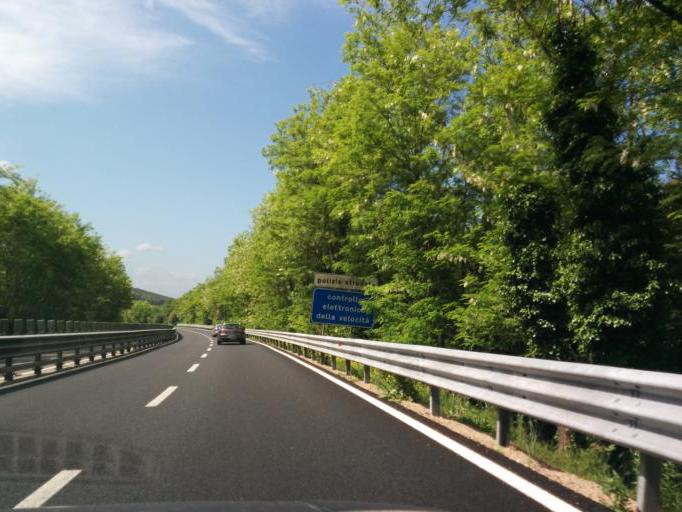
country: IT
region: Tuscany
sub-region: Province of Florence
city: Barberino Val d'Elsa
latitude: 43.5160
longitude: 11.1968
